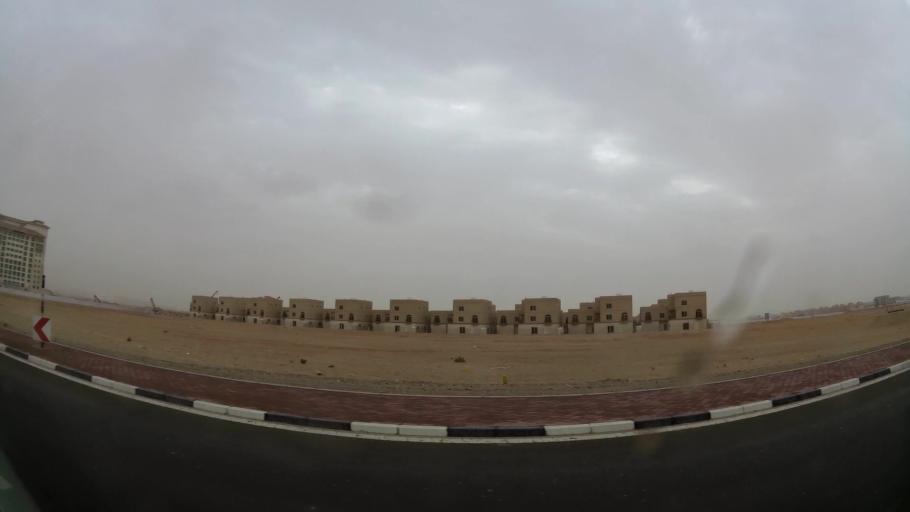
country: AE
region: Abu Dhabi
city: Abu Dhabi
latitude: 24.4421
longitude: 54.6045
